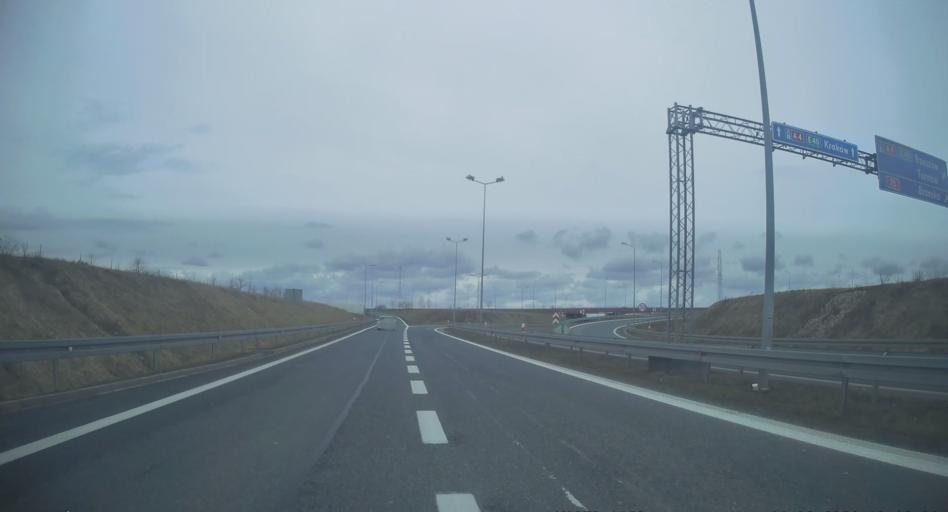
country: PL
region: Lesser Poland Voivodeship
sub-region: Powiat wielicki
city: Szarow
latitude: 49.9887
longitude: 20.2791
